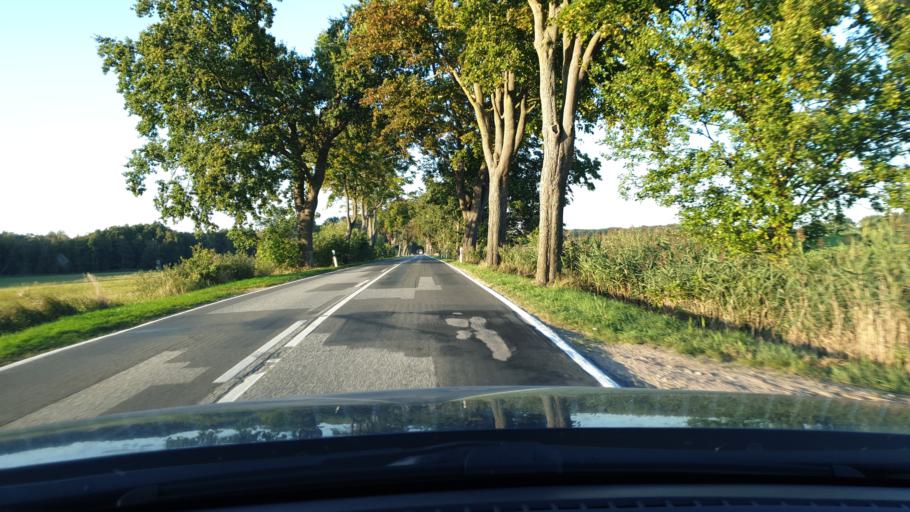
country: DE
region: Mecklenburg-Vorpommern
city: Wittenburg
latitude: 53.5597
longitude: 11.0950
